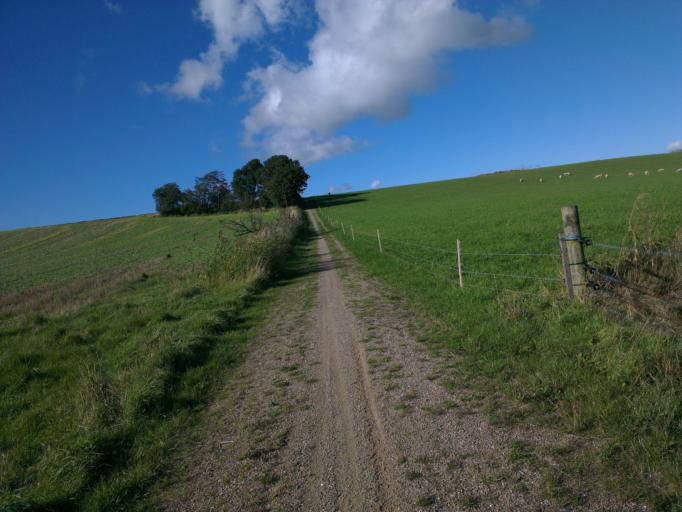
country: DK
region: Capital Region
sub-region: Frederikssund Kommune
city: Frederikssund
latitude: 55.8025
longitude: 12.0341
